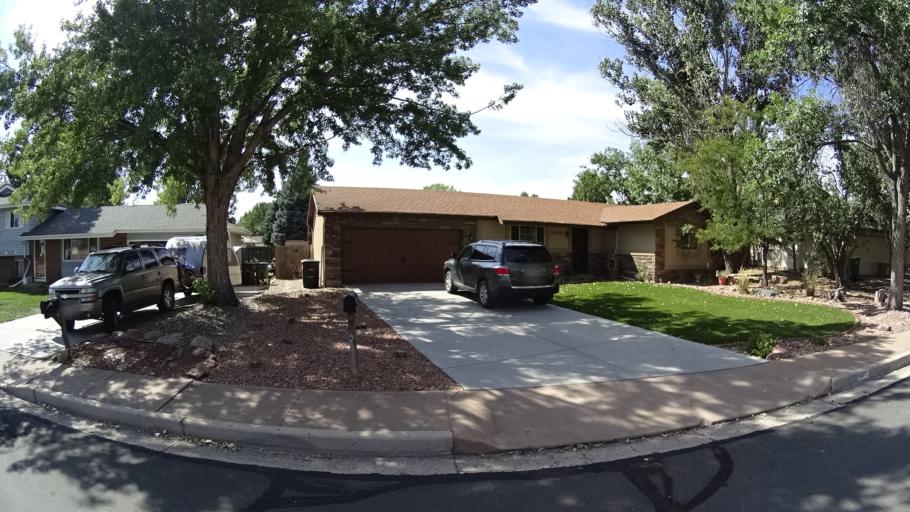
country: US
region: Colorado
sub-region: El Paso County
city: Cimarron Hills
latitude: 38.9008
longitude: -104.7592
